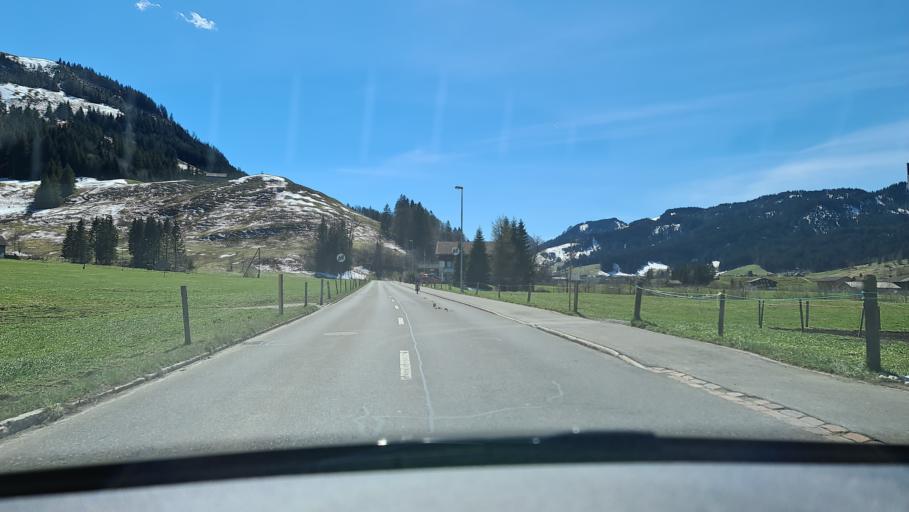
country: CH
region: Schwyz
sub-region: Bezirk Einsiedeln
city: Einsiedeln
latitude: 47.1140
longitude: 8.7362
